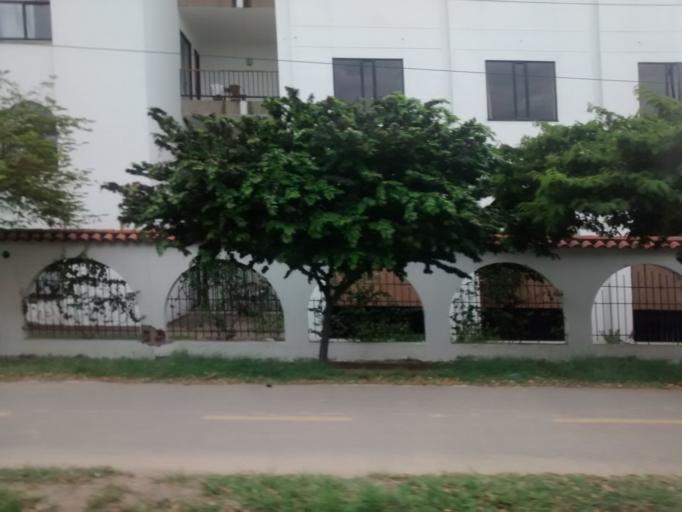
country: CO
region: Cundinamarca
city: Ricaurte
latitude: 4.2891
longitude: -74.7773
